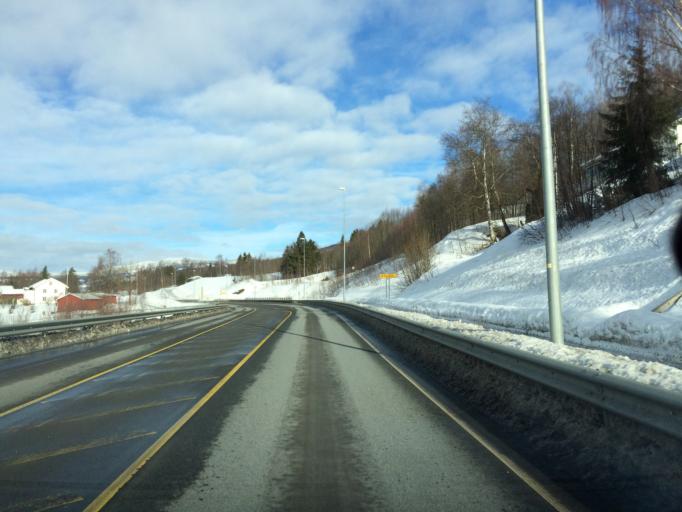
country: NO
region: Oppland
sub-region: Gausdal
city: Segalstad bru
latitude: 61.1892
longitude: 10.3178
